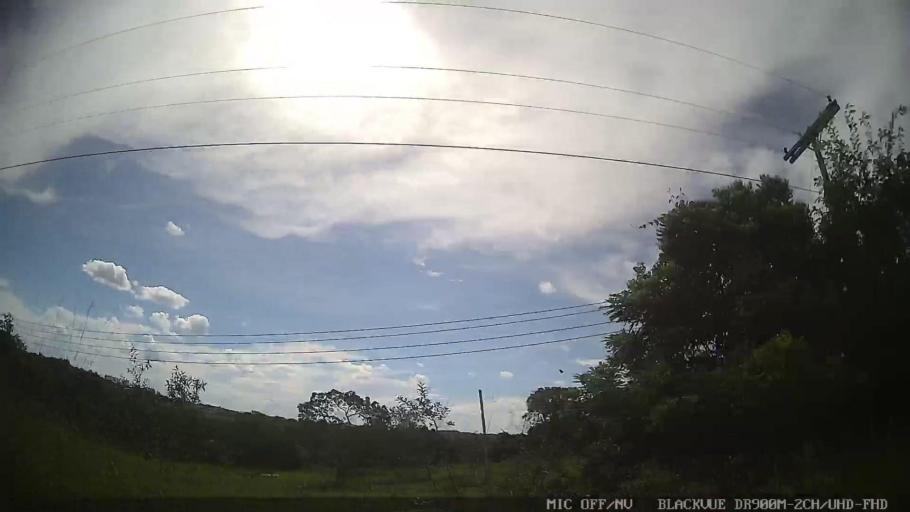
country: BR
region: Sao Paulo
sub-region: Conchas
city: Conchas
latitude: -22.9960
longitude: -47.9998
